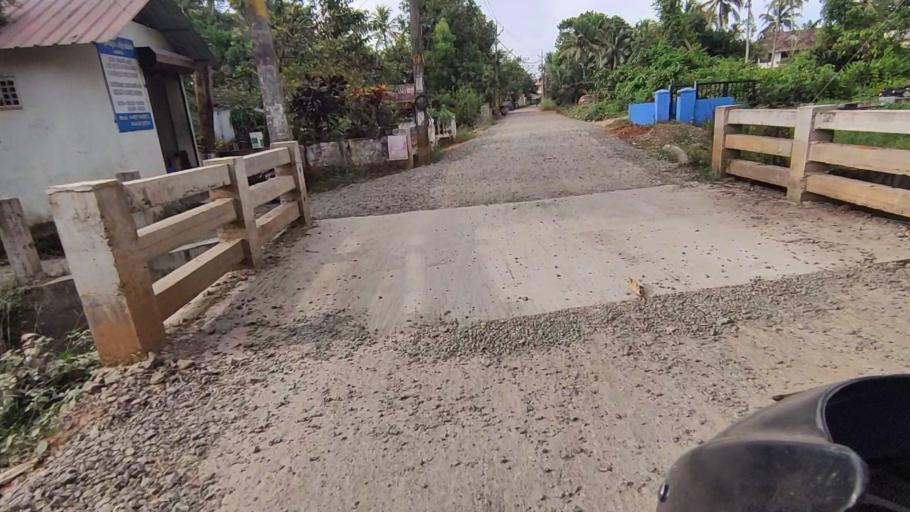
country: IN
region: Kerala
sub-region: Kottayam
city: Kottayam
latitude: 9.5833
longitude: 76.4914
